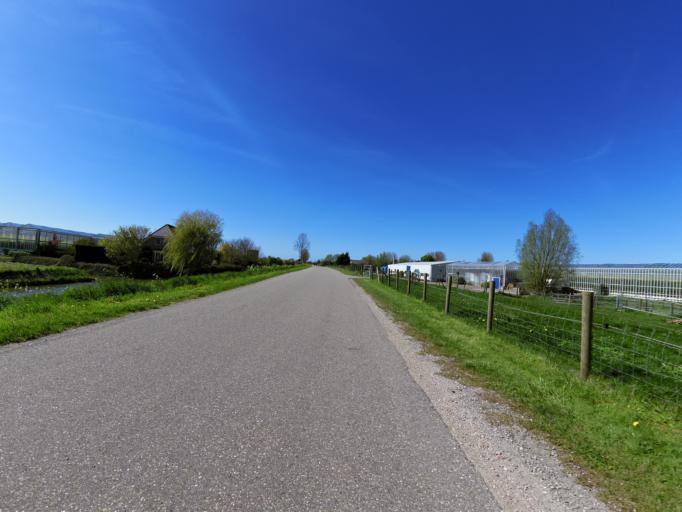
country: NL
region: South Holland
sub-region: Gemeente Brielle
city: Brielle
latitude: 51.8973
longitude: 4.1288
